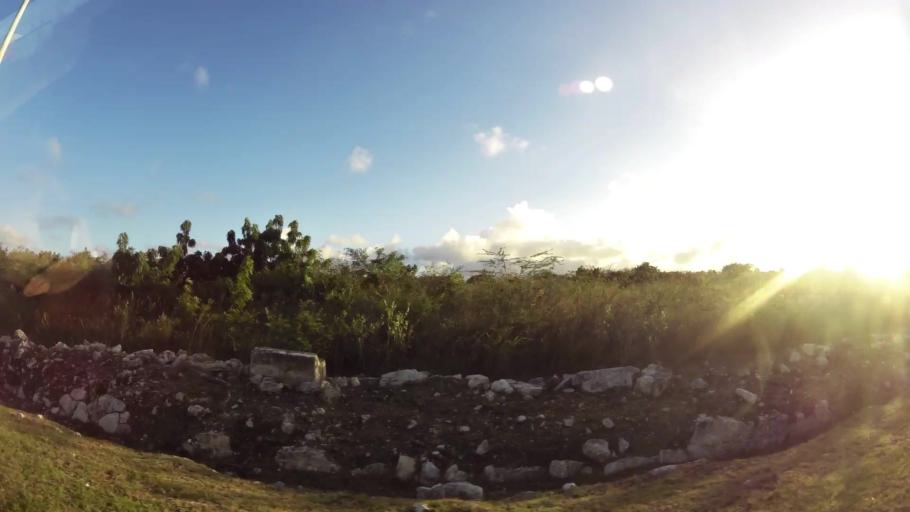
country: AG
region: Saint George
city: Piggotts
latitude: 17.1518
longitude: -61.7961
